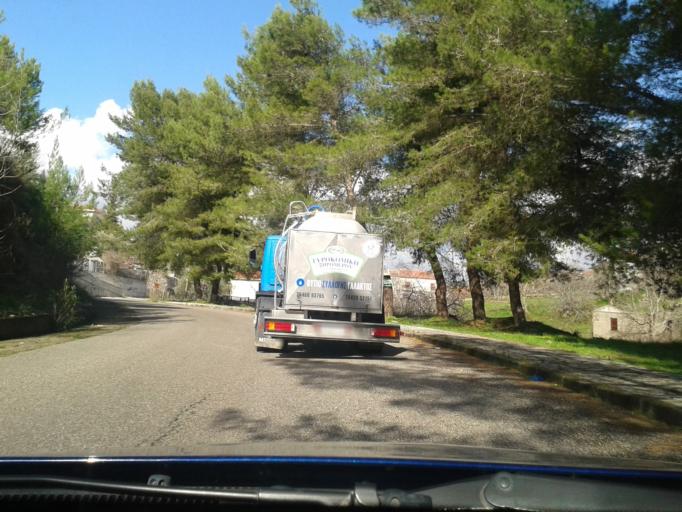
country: GR
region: West Greece
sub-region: Nomos Aitolias kai Akarnanias
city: Fitiai
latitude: 38.6918
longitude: 21.1843
